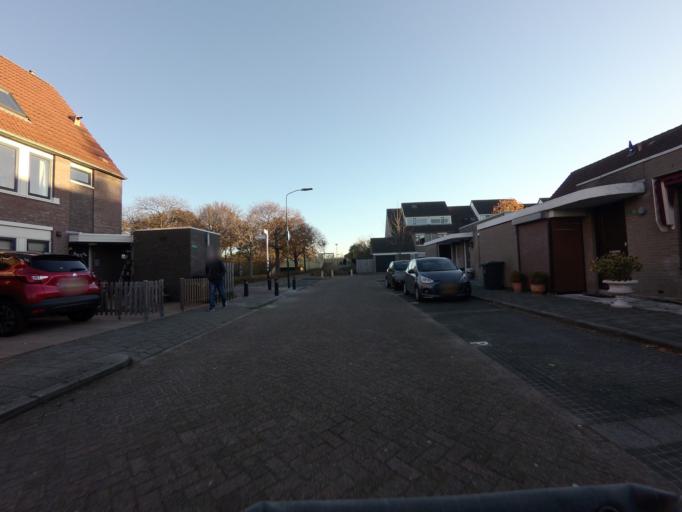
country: NL
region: Utrecht
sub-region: Stichtse Vecht
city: Spechtenkamp
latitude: 52.1434
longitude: 5.0155
